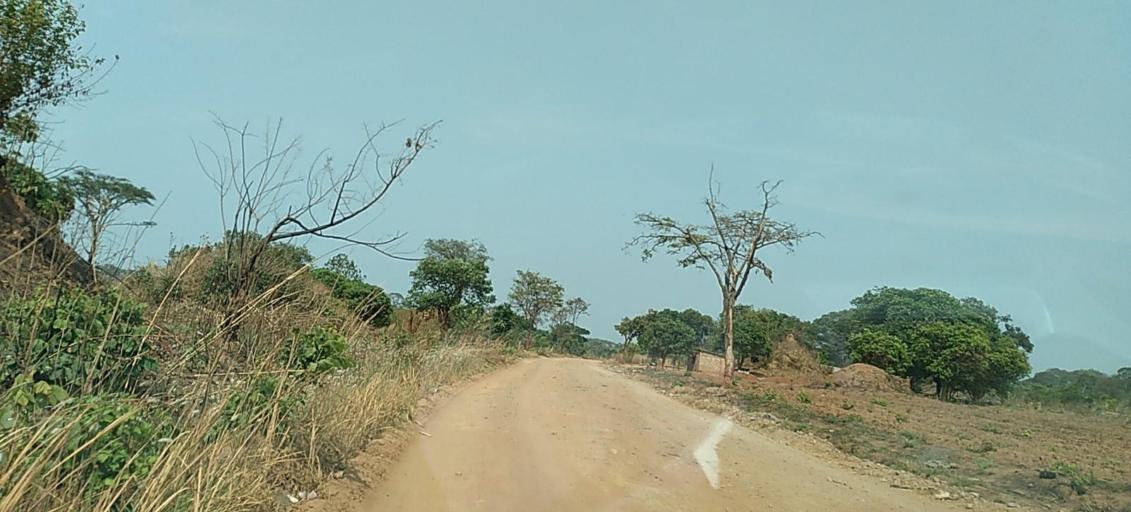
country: ZM
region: Copperbelt
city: Chililabombwe
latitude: -12.3390
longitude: 27.7199
